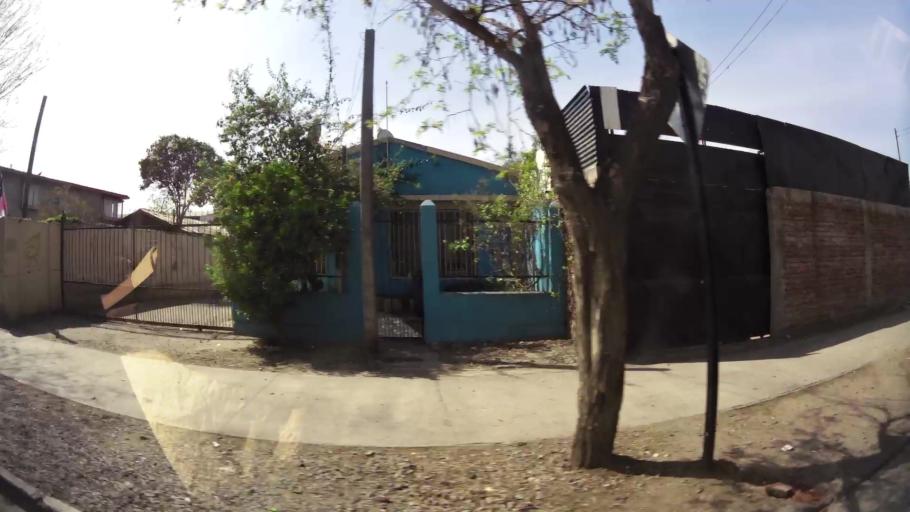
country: CL
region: Santiago Metropolitan
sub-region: Provincia de Santiago
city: Lo Prado
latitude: -33.4368
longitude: -70.7634
